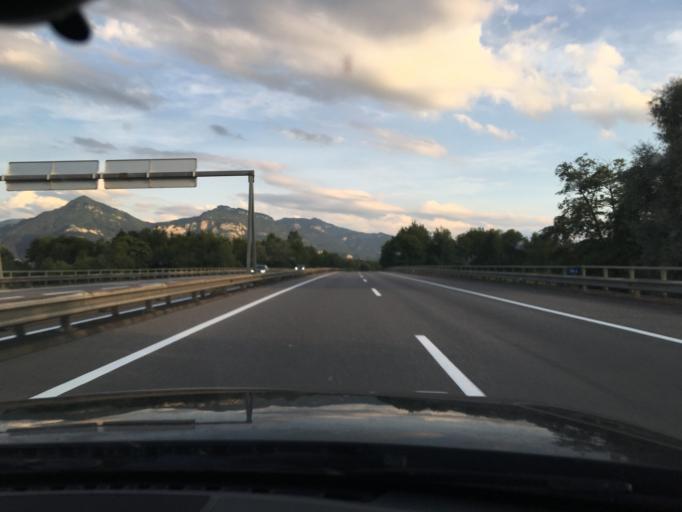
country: AT
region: Vorarlberg
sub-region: Politischer Bezirk Dornbirn
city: Dornbirn
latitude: 47.4416
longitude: 9.7229
